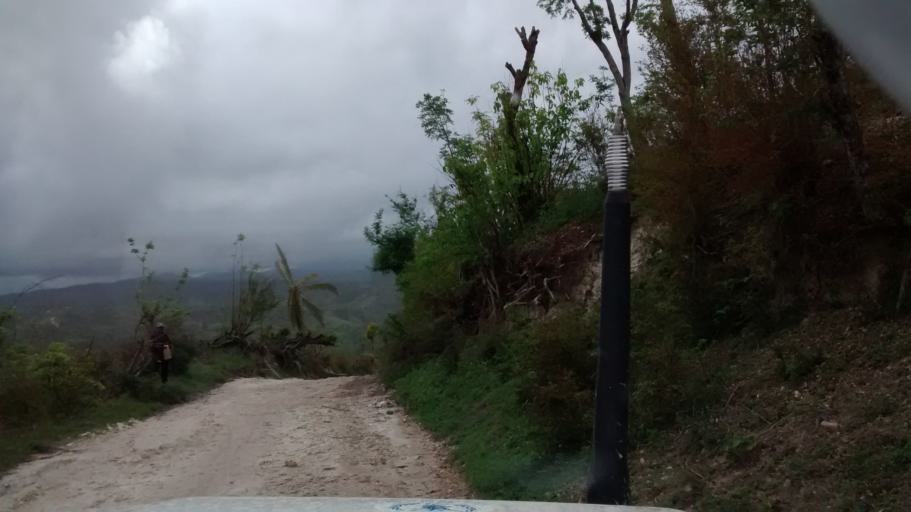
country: HT
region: Grandans
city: Jeremie
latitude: 18.5825
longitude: -74.1492
